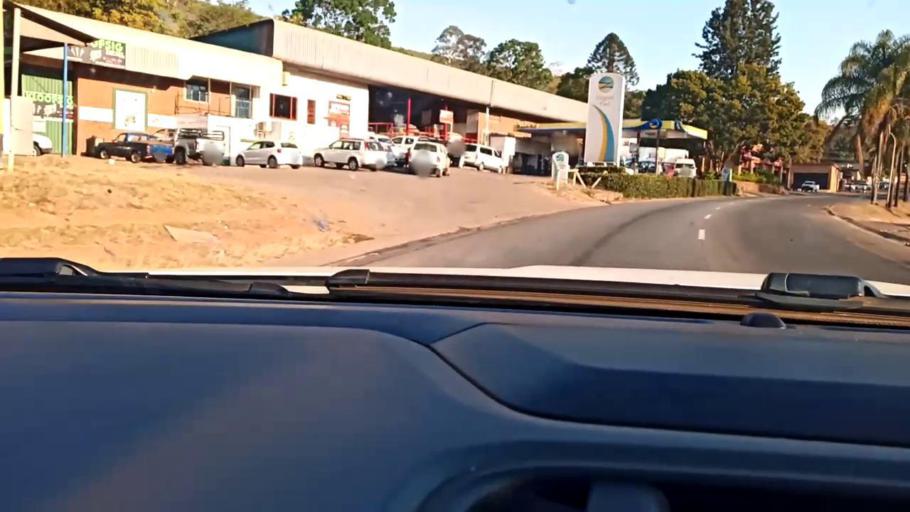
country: ZA
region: Limpopo
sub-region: Mopani District Municipality
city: Duiwelskloof
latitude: -23.6928
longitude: 30.1467
